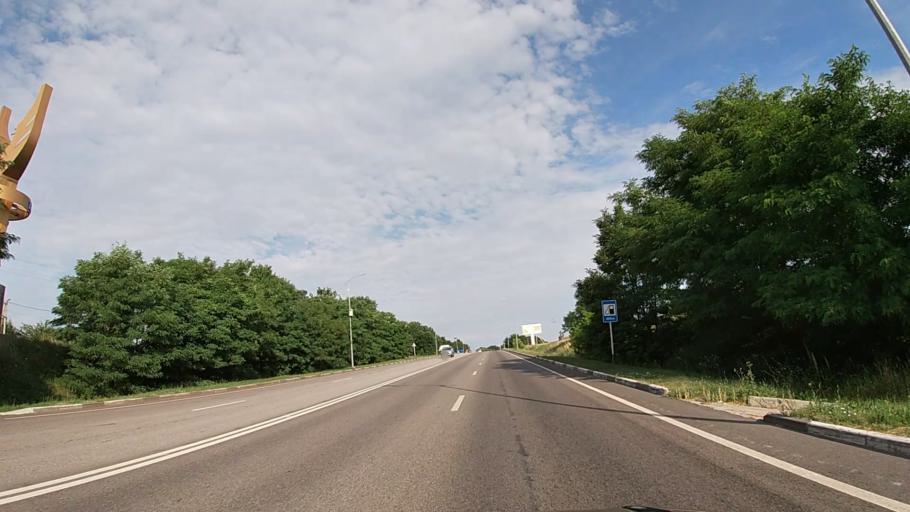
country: RU
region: Belgorod
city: Severnyy
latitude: 50.6369
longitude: 36.4487
